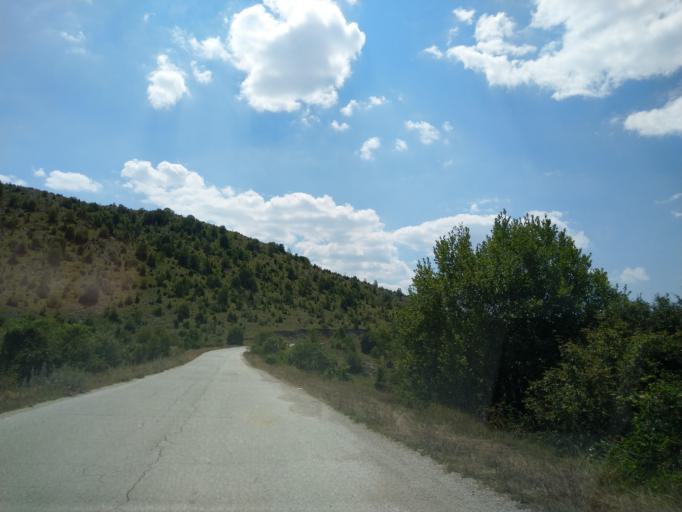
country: RS
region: Central Serbia
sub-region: Zlatiborski Okrug
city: Nova Varos
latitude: 43.4275
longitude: 19.9463
